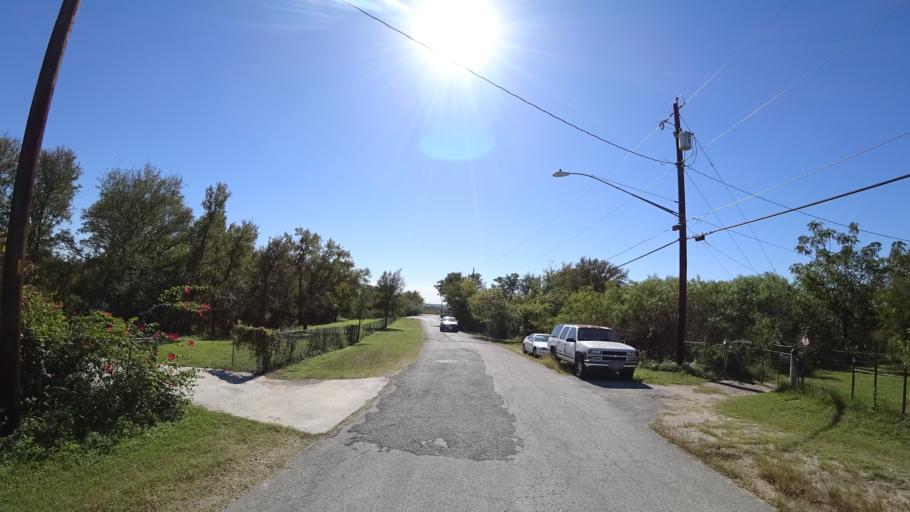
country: US
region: Texas
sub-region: Travis County
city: Hornsby Bend
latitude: 30.2815
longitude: -97.6423
